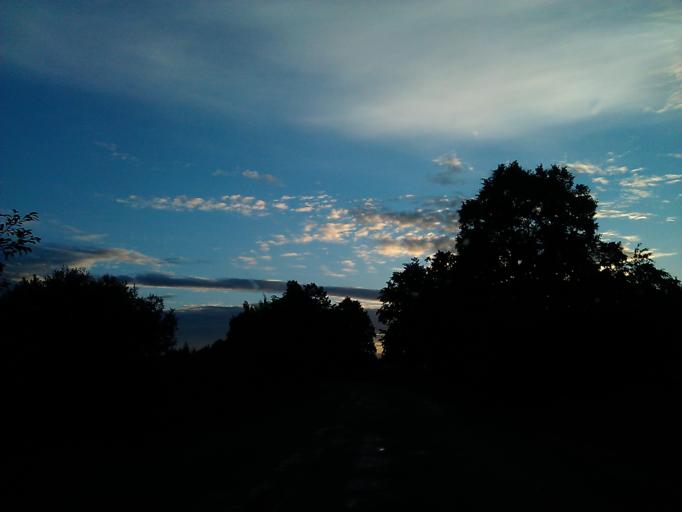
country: LV
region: Sigulda
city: Sigulda
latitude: 57.2503
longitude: 24.8722
